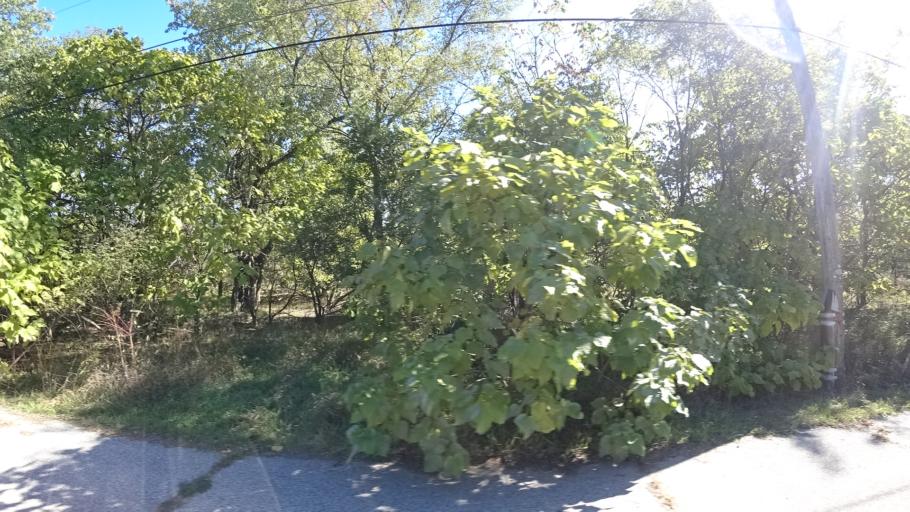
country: US
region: Indiana
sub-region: LaPorte County
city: Michigan City
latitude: 41.7035
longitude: -86.9108
